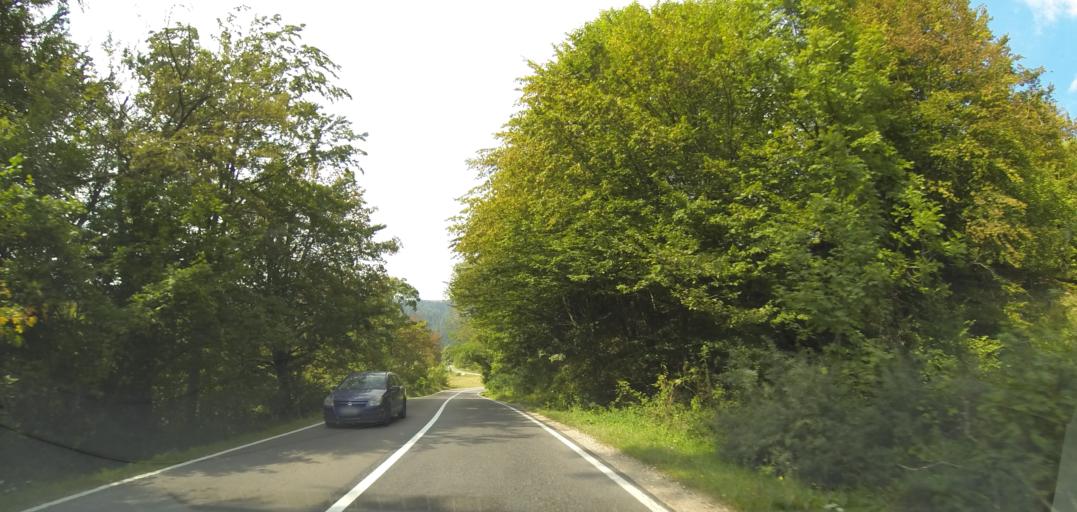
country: RO
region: Brasov
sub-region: Comuna Tarlungeni
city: Zizin
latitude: 45.5556
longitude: 25.8000
